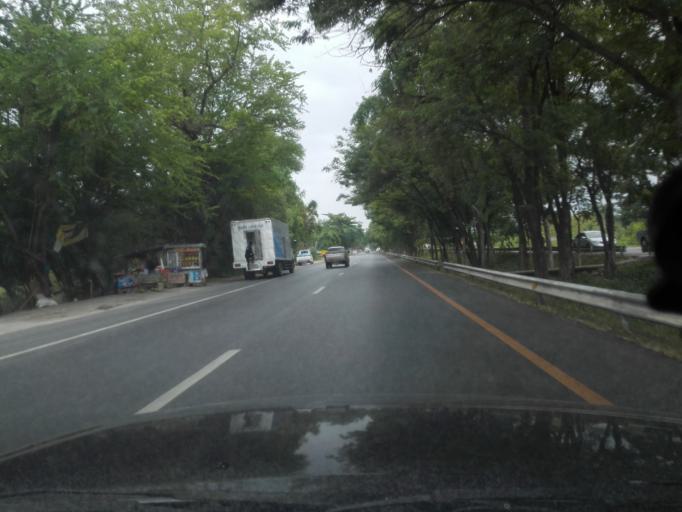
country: TH
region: Nakhon Sawan
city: Nakhon Sawan
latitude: 15.7324
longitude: 100.0306
